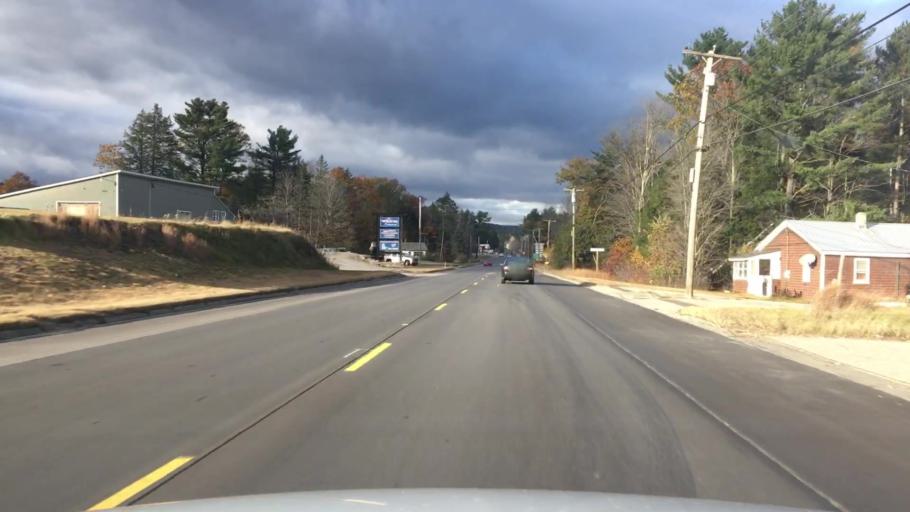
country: US
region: Maine
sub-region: Androscoggin County
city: Livermore
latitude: 44.3710
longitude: -70.2508
